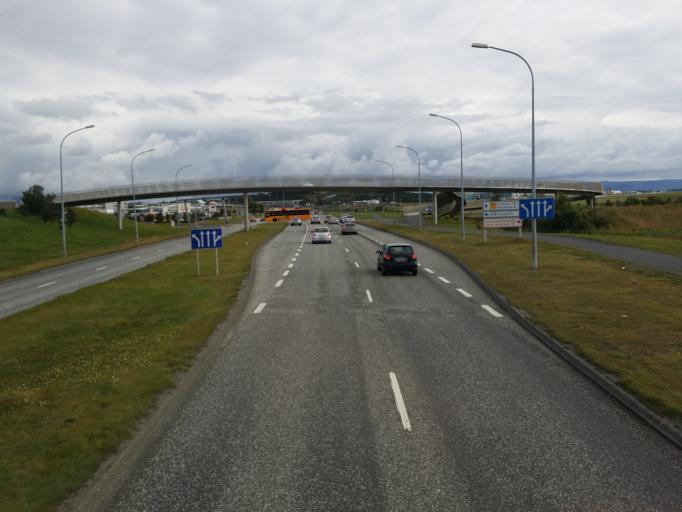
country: IS
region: Capital Region
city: Kopavogur
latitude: 64.1397
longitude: -21.9422
